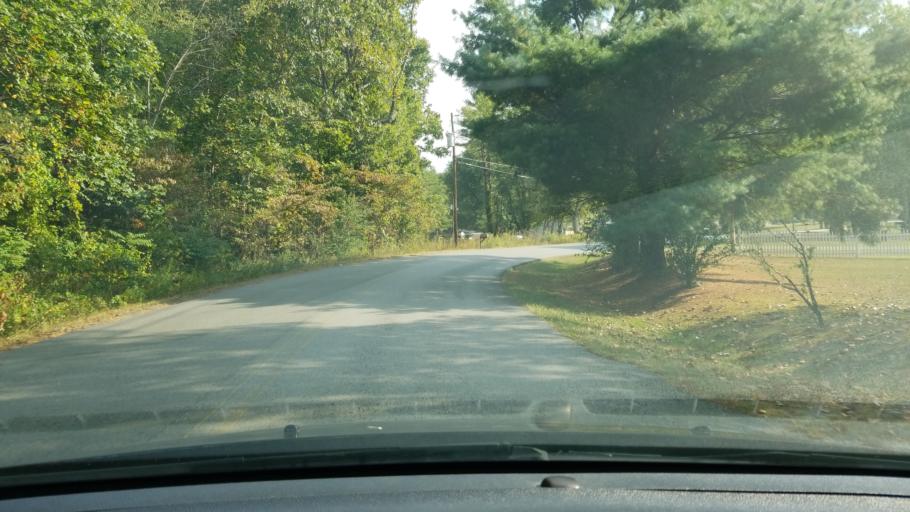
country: US
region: Tennessee
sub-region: Cumberland County
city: Crossville
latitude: 35.9471
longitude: -85.0935
